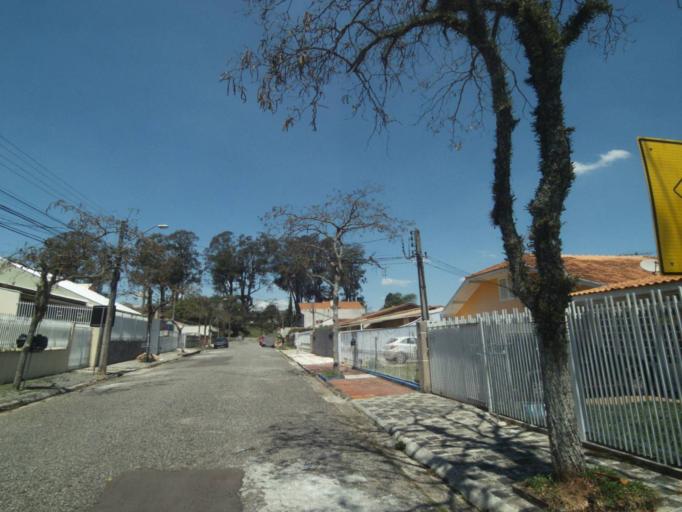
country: BR
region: Parana
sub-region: Pinhais
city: Pinhais
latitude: -25.3951
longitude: -49.2169
